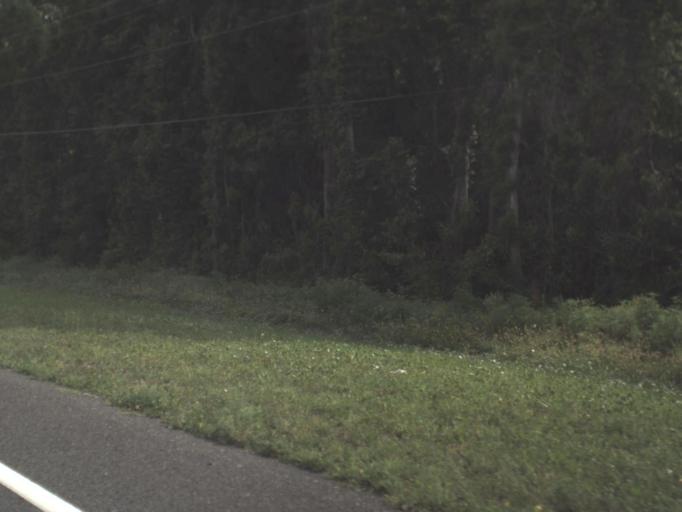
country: US
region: Florida
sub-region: Clay County
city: Orange Park
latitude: 30.1311
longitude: -81.7030
